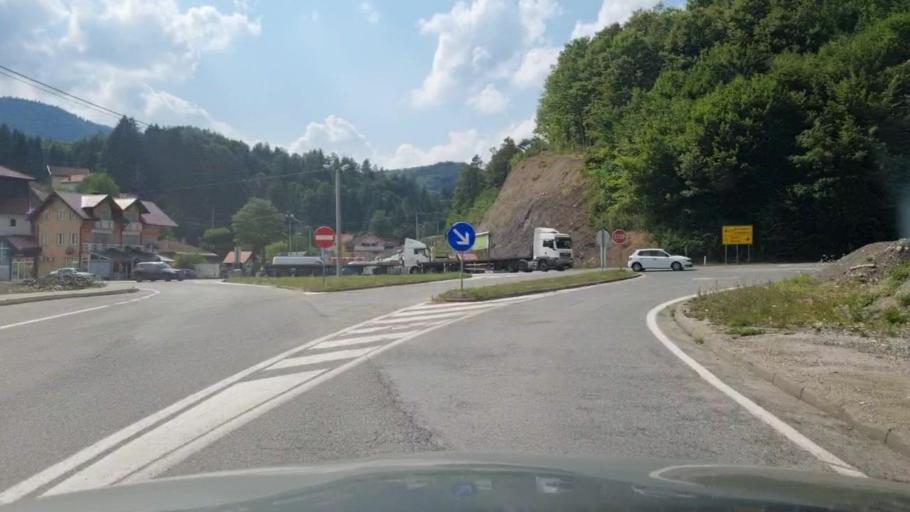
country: BA
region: Federation of Bosnia and Herzegovina
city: Kladanj
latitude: 44.2410
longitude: 18.7051
